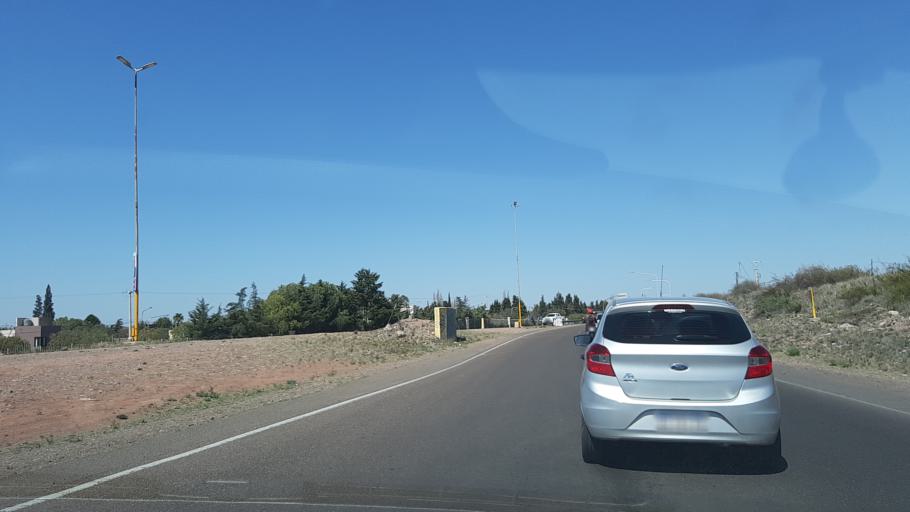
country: AR
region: Mendoza
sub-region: Departamento de Godoy Cruz
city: Godoy Cruz
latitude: -32.9710
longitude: -68.8816
